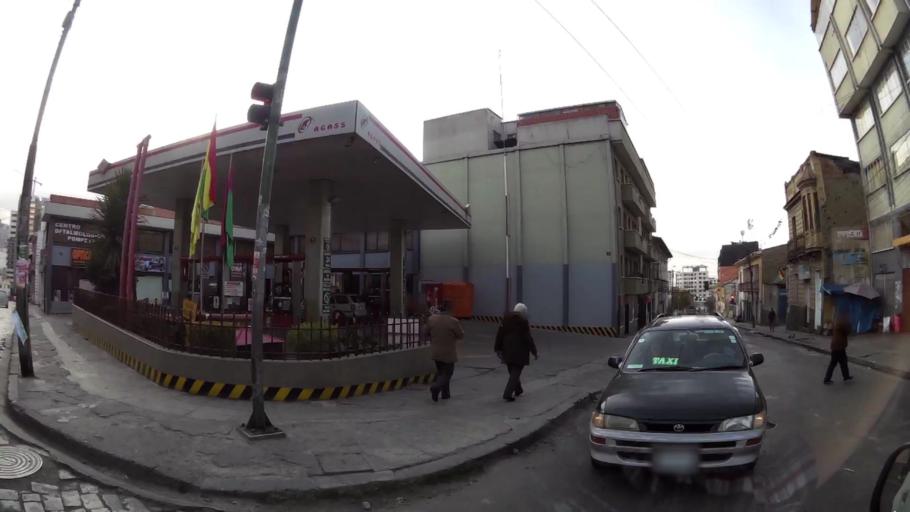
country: BO
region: La Paz
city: La Paz
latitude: -16.5020
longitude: -68.1364
